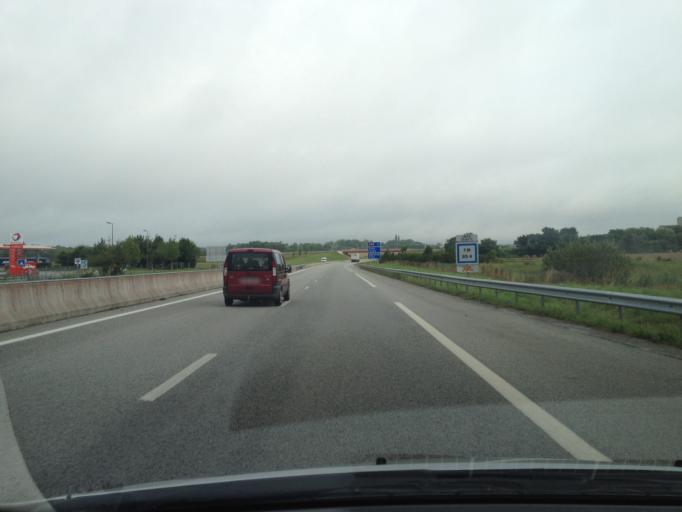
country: FR
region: Lower Normandy
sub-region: Departement de l'Orne
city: Valframbert
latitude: 48.4568
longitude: 0.1285
